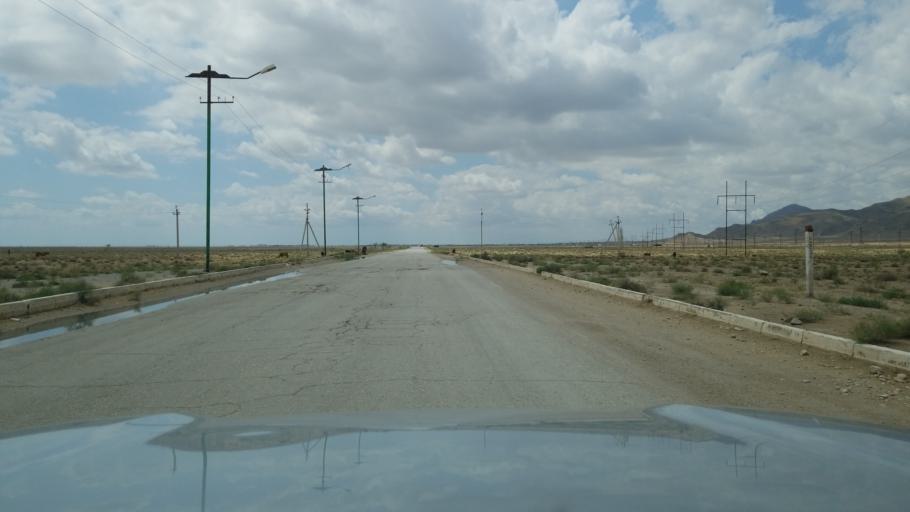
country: TM
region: Balkan
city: Balkanabat
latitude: 39.4804
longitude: 54.4543
